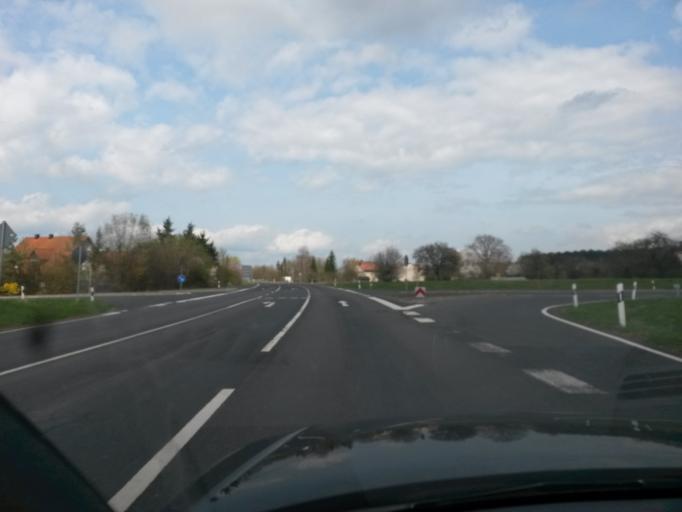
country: DE
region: Bavaria
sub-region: Regierungsbezirk Unterfranken
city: Volkach
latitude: 49.8595
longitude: 10.2416
